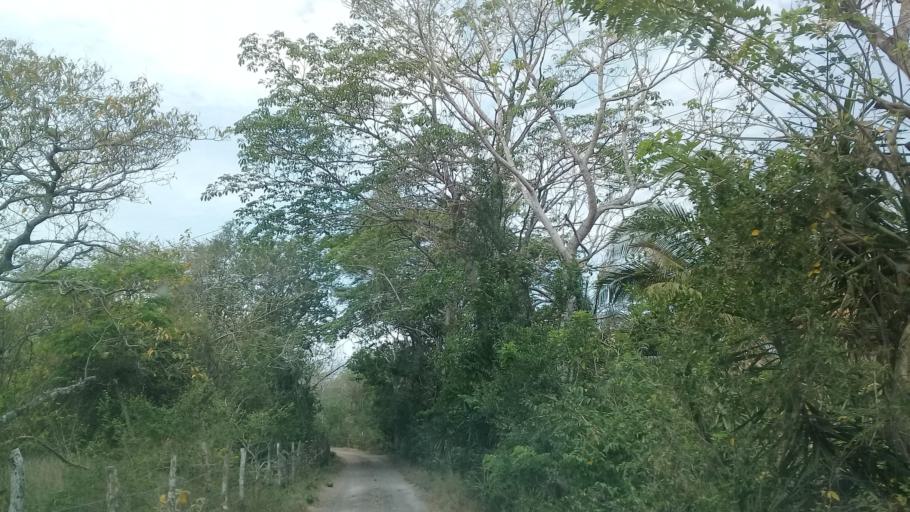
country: MX
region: Veracruz
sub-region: Veracruz
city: Delfino Victoria (Santa Fe)
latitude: 19.1754
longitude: -96.3032
